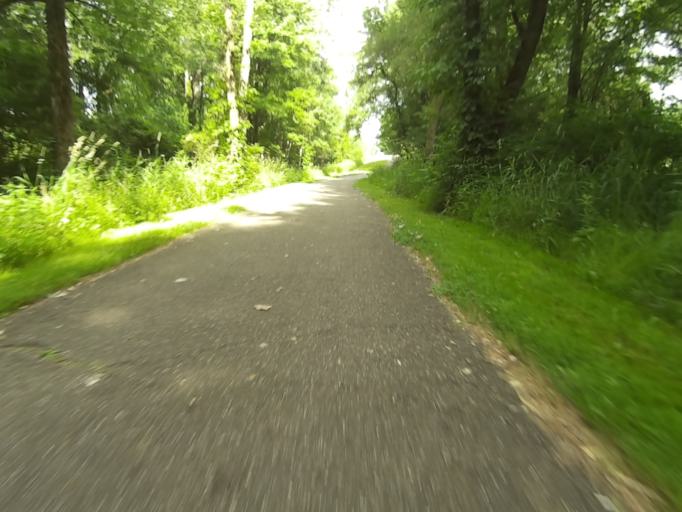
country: US
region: Ohio
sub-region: Portage County
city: Kent
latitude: 41.1885
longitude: -81.3883
